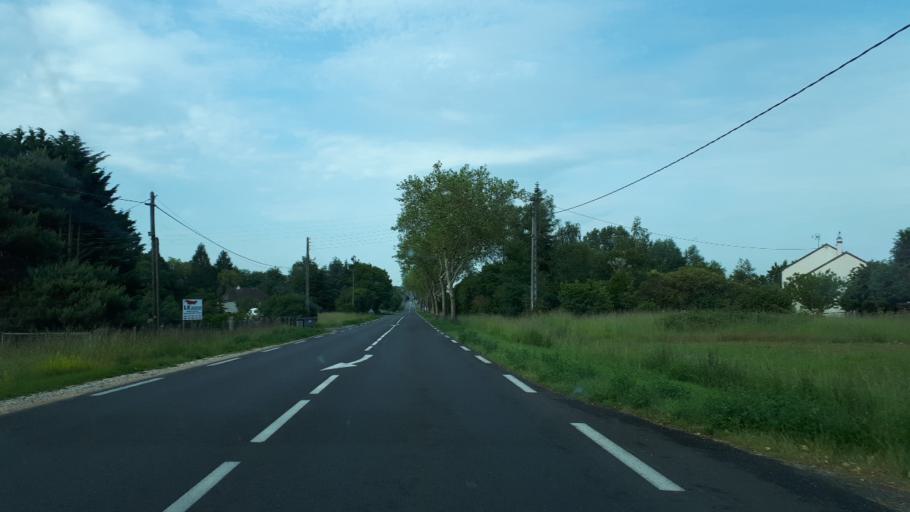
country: FR
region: Centre
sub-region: Departement d'Indre-et-Loire
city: Monnaie
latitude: 47.5092
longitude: 0.8018
